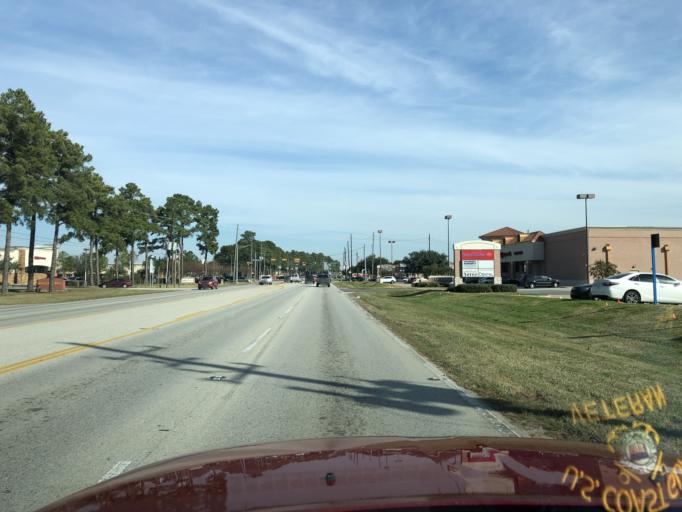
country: US
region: Texas
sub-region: Harris County
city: Tomball
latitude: 30.0316
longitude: -95.5563
